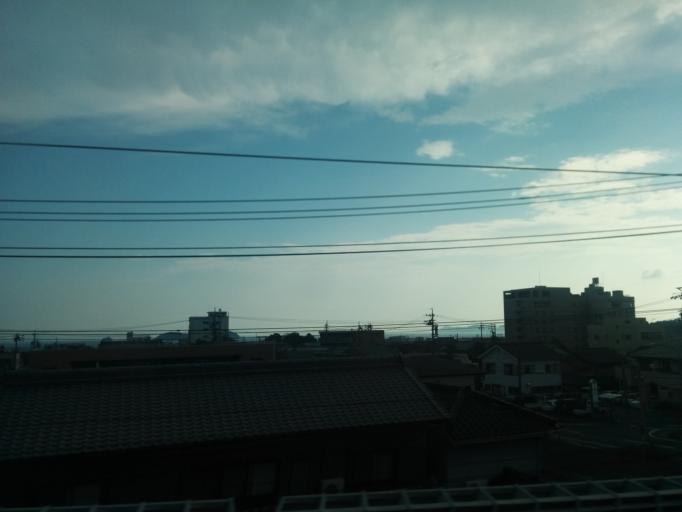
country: JP
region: Aichi
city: Gamagori
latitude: 34.8201
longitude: 137.2511
